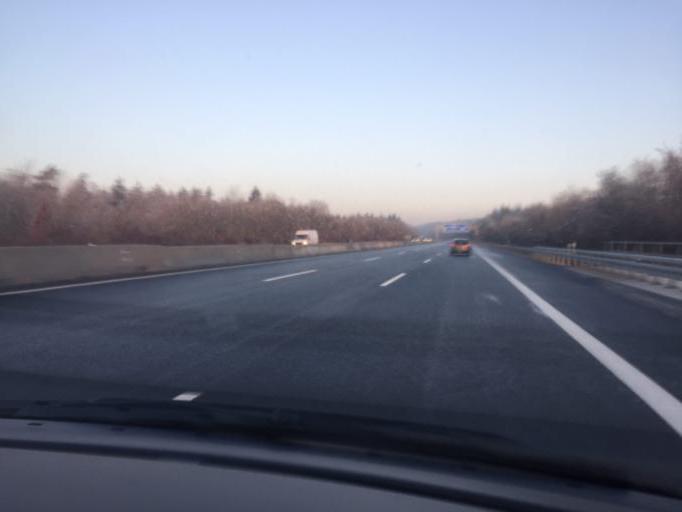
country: DE
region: Baden-Wuerttemberg
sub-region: Freiburg Region
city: Muhlhausen-Ehingen
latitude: 47.8405
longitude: 8.8155
